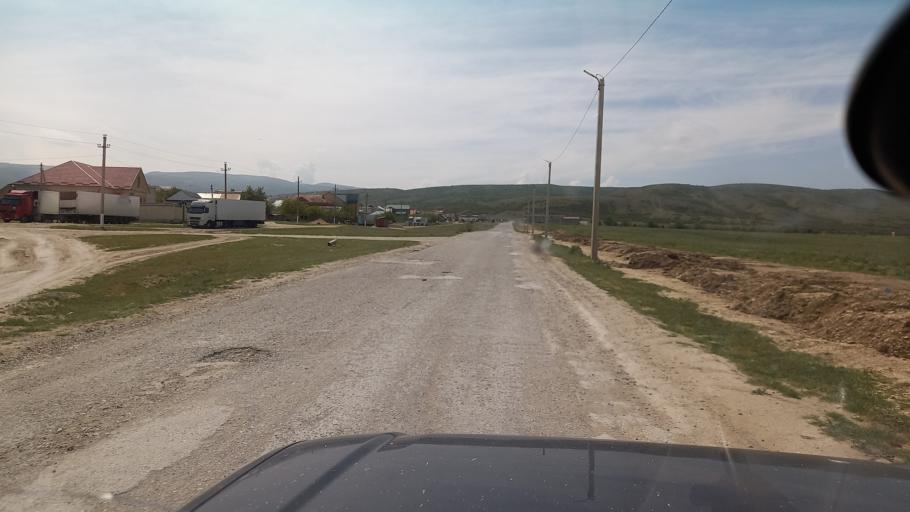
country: RU
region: Dagestan
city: Gurbuki
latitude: 42.6174
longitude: 47.5930
